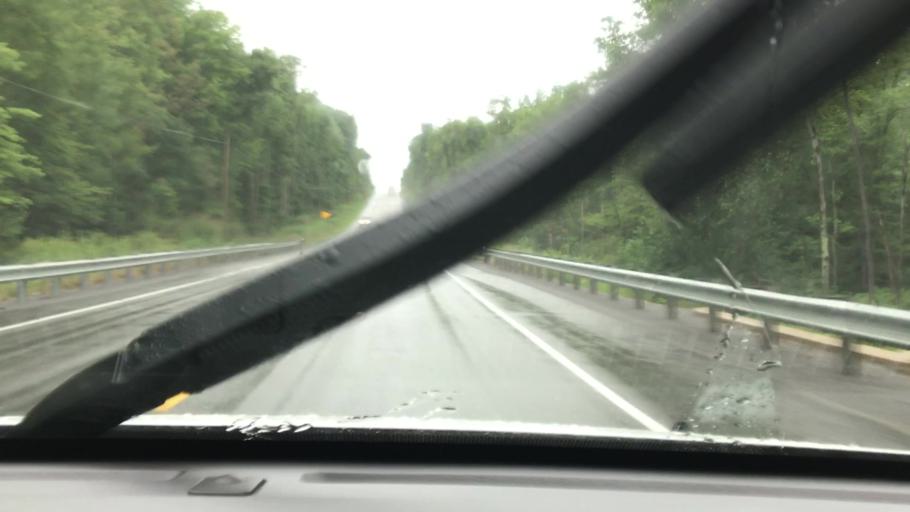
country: US
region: Pennsylvania
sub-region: Clearfield County
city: Osceola Mills
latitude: 40.8344
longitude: -78.2240
